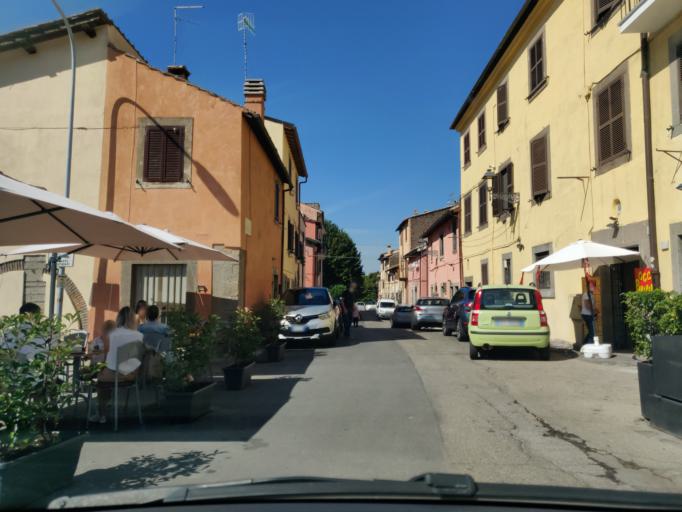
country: IT
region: Latium
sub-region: Provincia di Viterbo
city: Viterbo
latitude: 42.4301
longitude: 12.1290
